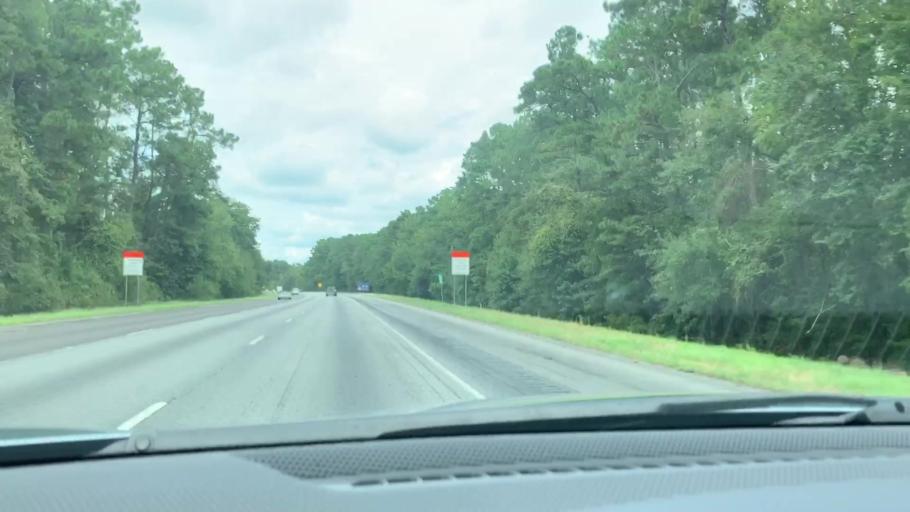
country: US
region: Georgia
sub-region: Bryan County
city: Richmond Hill
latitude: 31.8953
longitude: -81.3240
